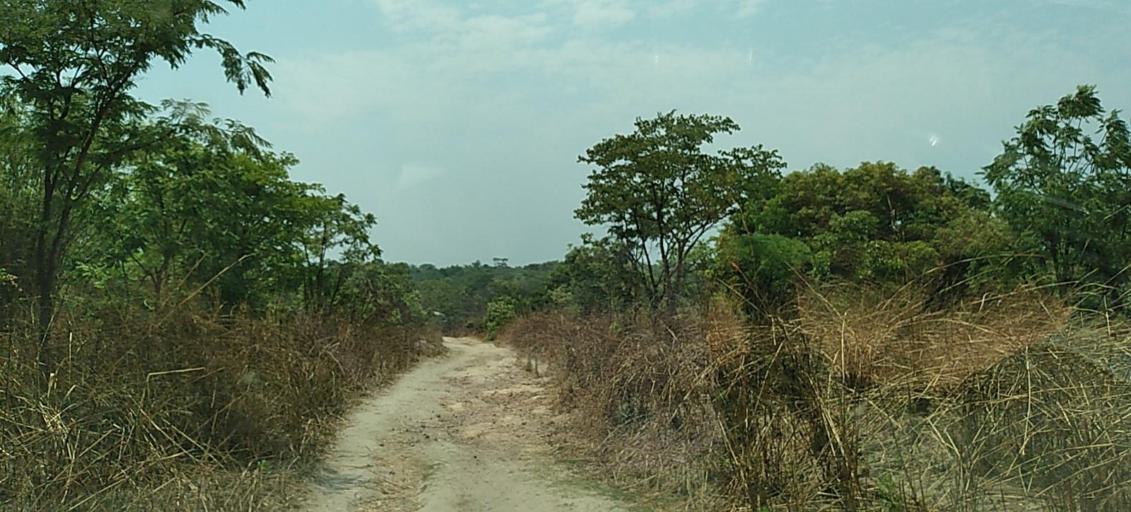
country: ZM
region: Copperbelt
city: Kalulushi
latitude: -12.9459
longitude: 28.1277
